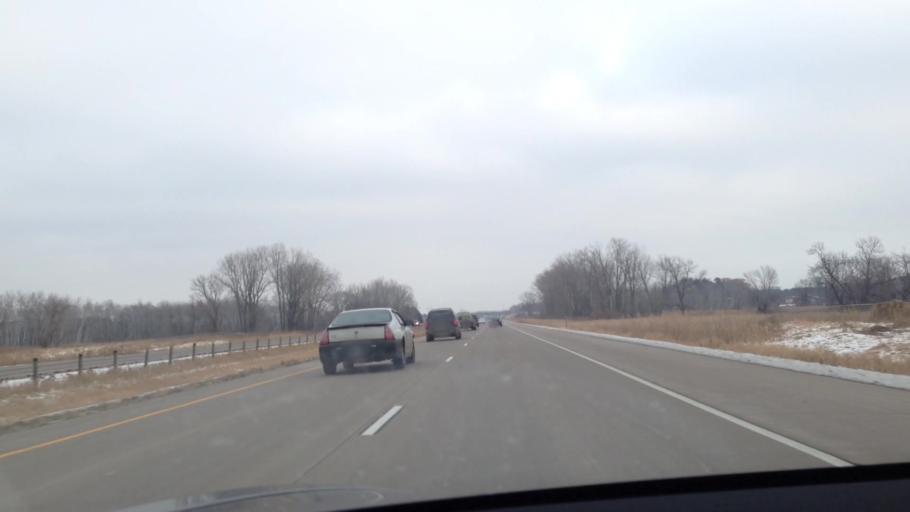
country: US
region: Minnesota
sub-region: Anoka County
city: Lino Lakes
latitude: 45.1893
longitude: -93.0844
